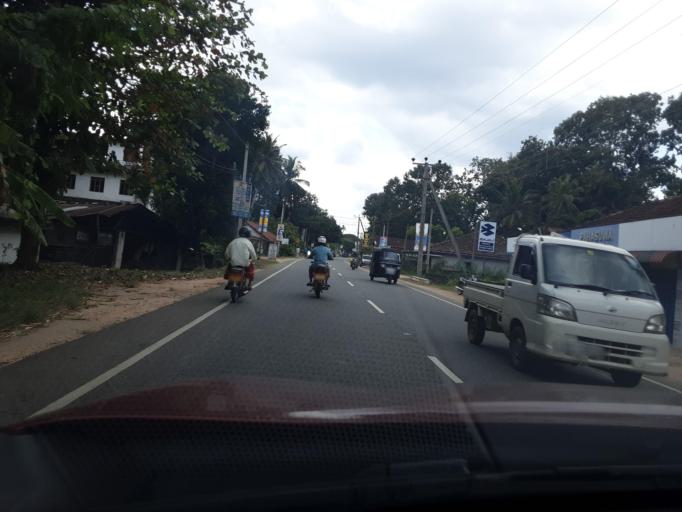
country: LK
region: North Western
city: Kurunegala
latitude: 7.4360
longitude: 80.2099
